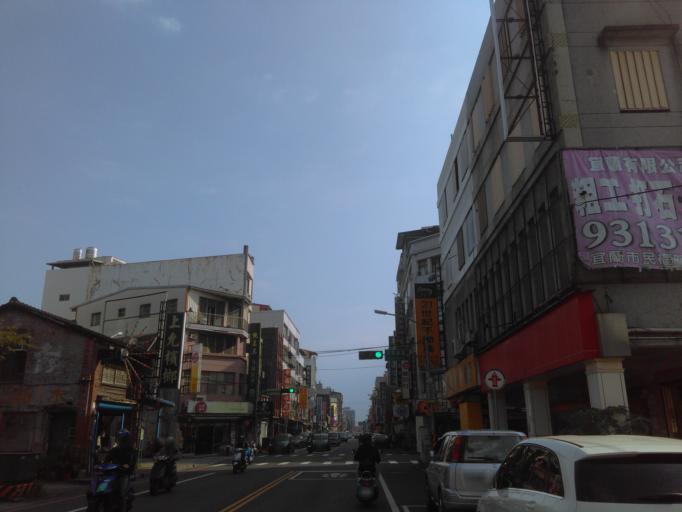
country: TW
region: Taiwan
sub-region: Yilan
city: Yilan
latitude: 24.7515
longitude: 121.7533
